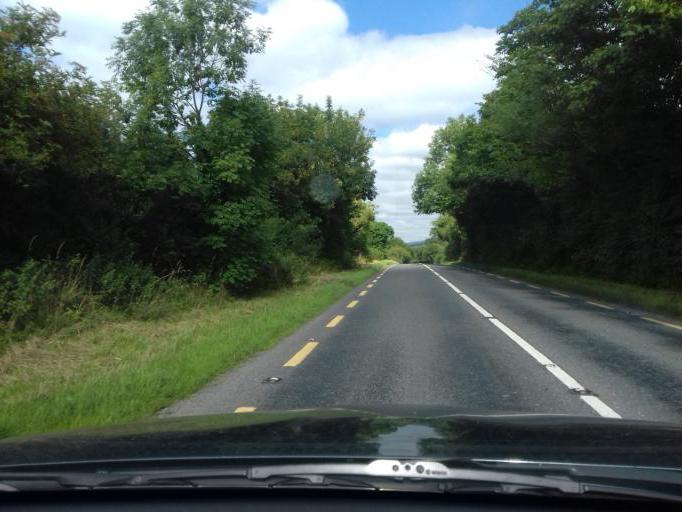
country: IE
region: Leinster
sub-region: Wicklow
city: Baltinglass
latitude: 52.9821
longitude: -6.6630
